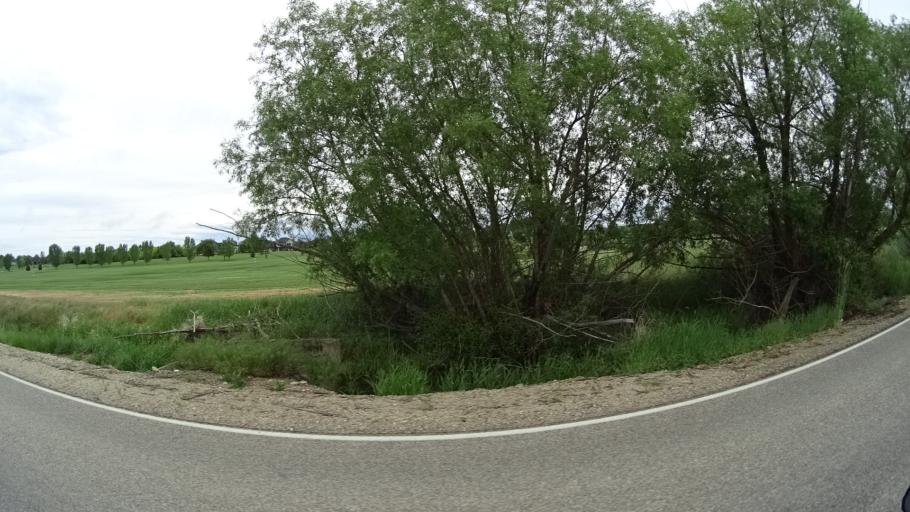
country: US
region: Idaho
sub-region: Ada County
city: Star
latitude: 43.7180
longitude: -116.4684
